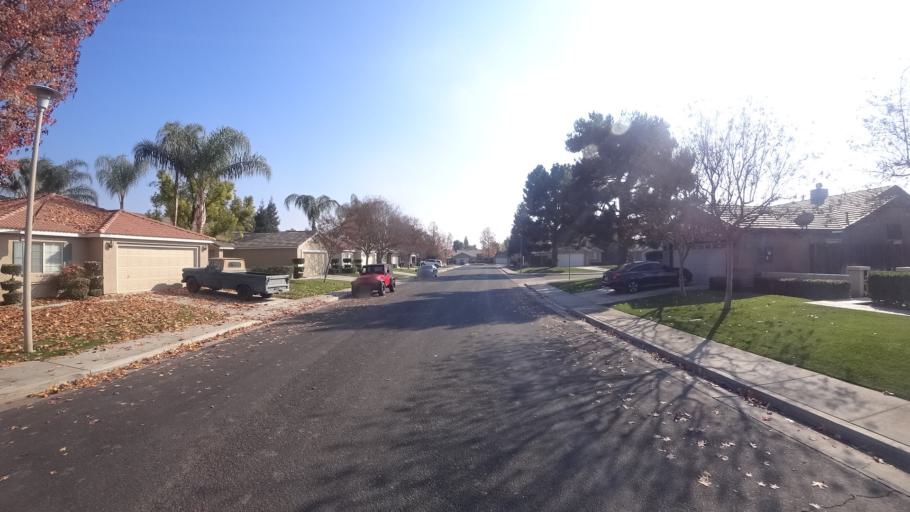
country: US
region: California
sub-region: Kern County
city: Greenacres
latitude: 35.3091
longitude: -119.0807
